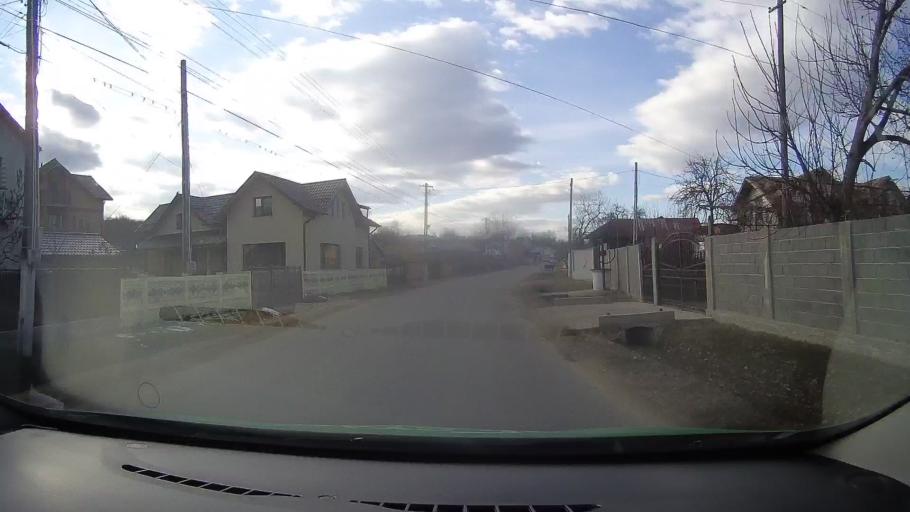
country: RO
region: Dambovita
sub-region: Comuna Ulmi
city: Ulmi
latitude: 44.8839
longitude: 25.5123
